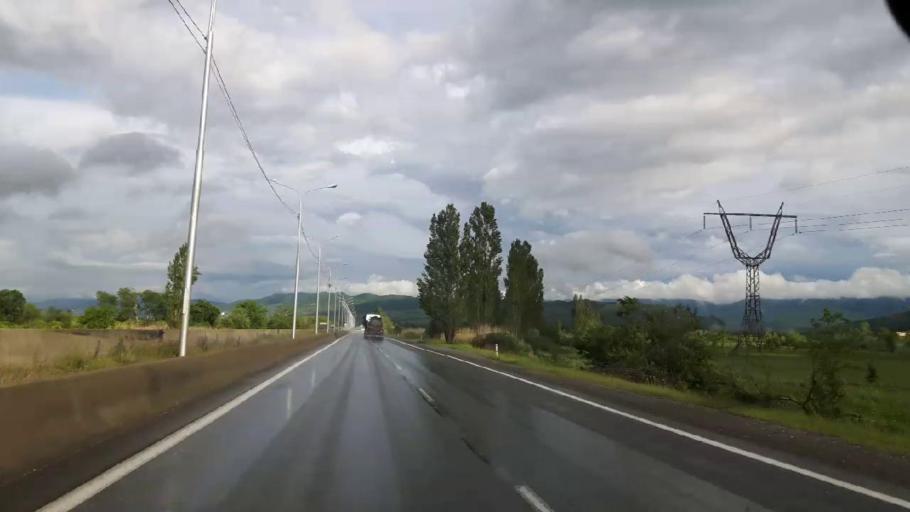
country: GE
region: Shida Kartli
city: Kaspi
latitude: 41.9236
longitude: 44.5418
